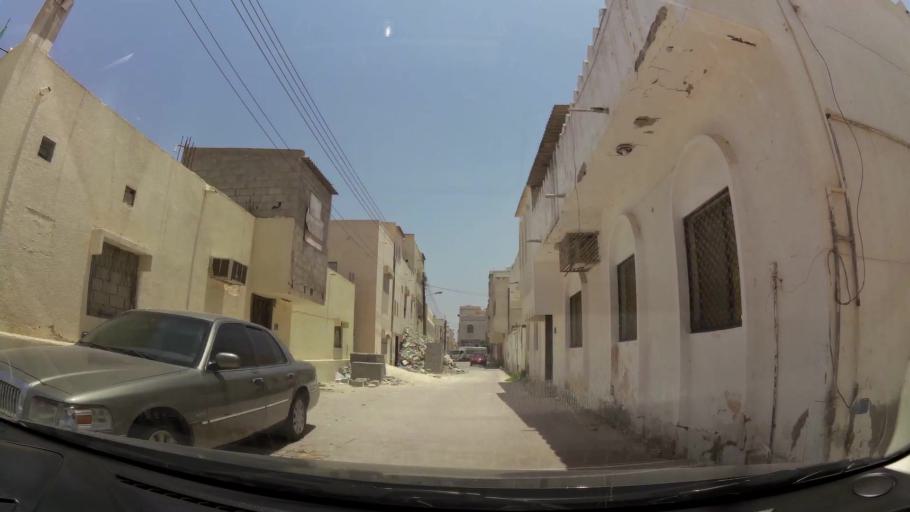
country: OM
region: Zufar
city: Salalah
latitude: 17.0144
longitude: 54.1023
